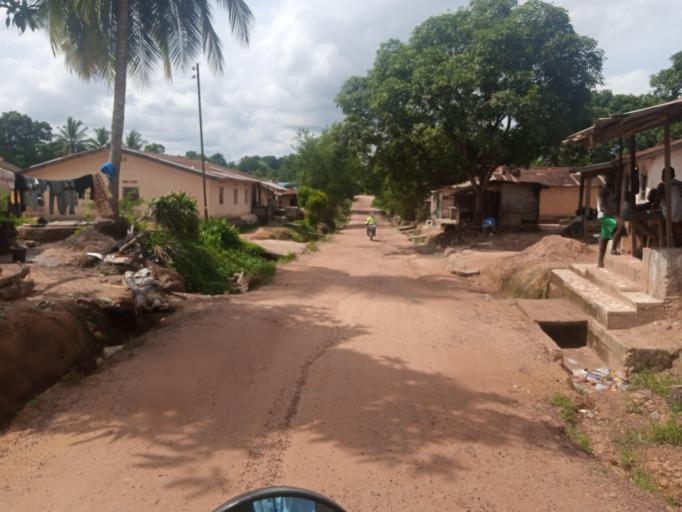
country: SL
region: Southern Province
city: Bo
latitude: 7.9642
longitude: -11.7544
